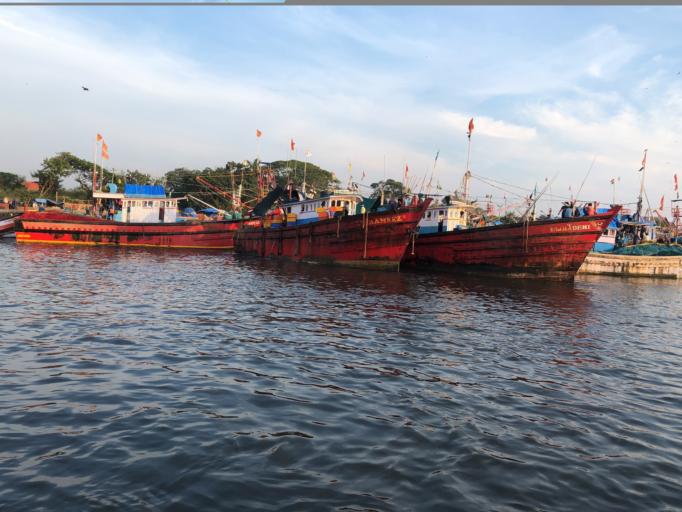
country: IN
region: Karnataka
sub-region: Dakshina Kannada
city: Ullal
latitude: 12.8525
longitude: 74.8324
